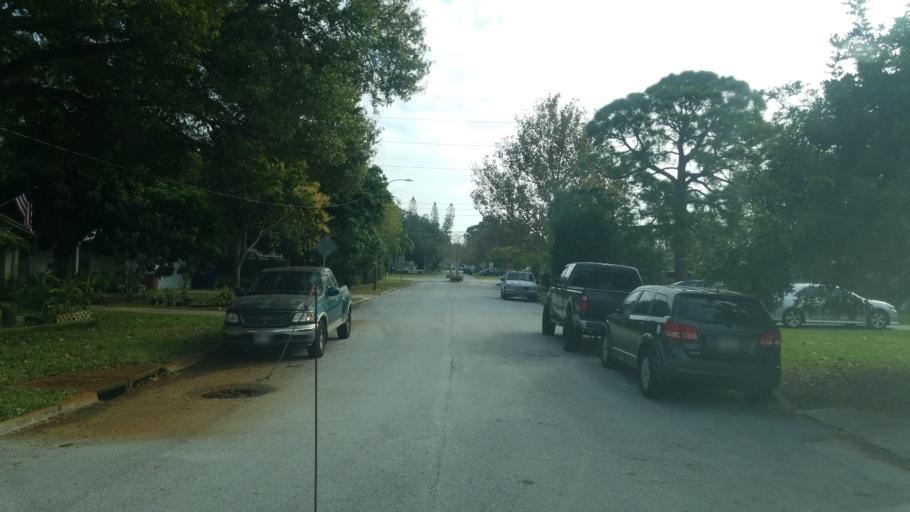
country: US
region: Florida
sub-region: Pinellas County
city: Saint Petersburg
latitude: 27.7956
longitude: -82.6724
